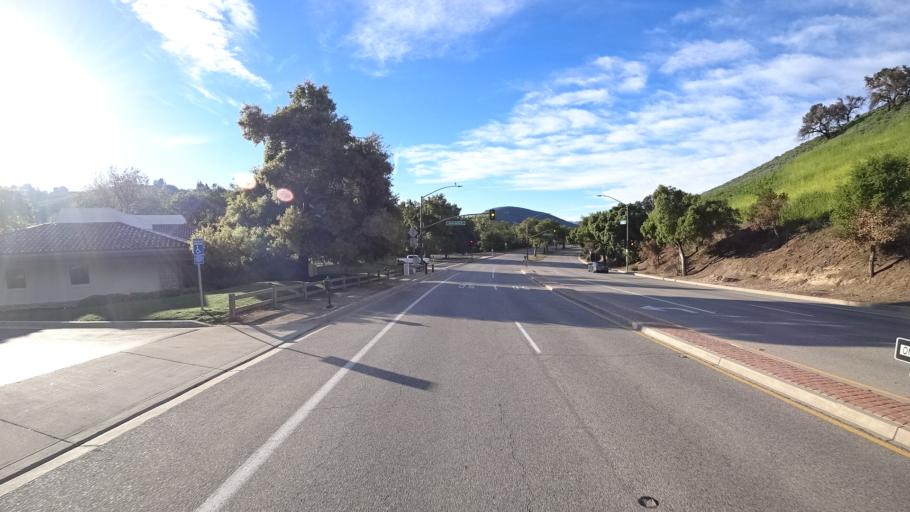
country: US
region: California
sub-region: Ventura County
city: Thousand Oaks
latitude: 34.1892
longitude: -118.8221
